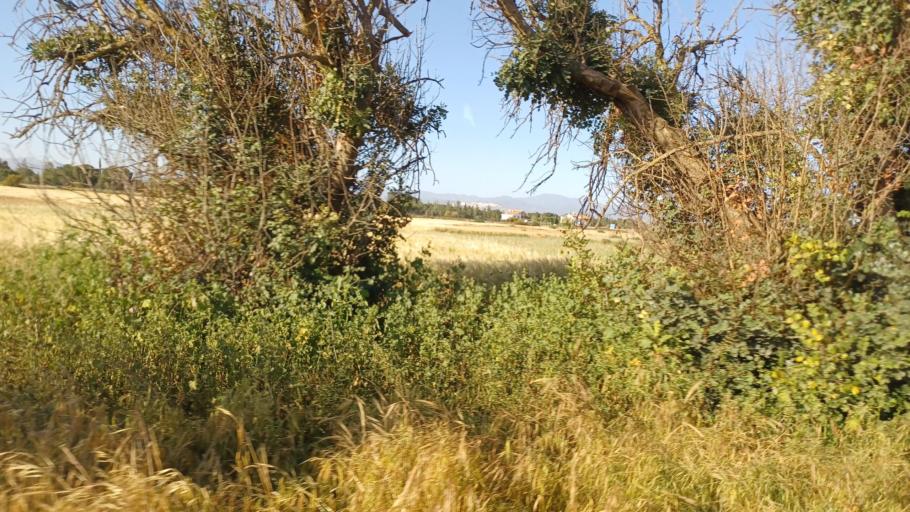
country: CY
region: Lefkosia
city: Kokkinotrimithia
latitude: 35.1497
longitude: 33.1823
